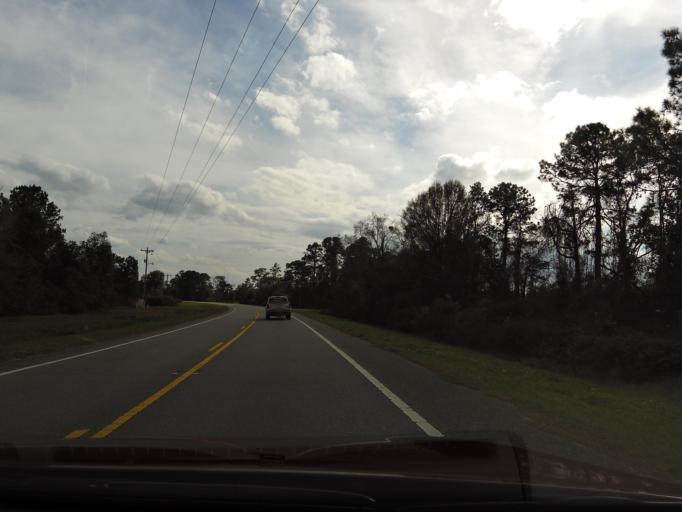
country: US
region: Florida
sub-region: Volusia County
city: De Leon Springs
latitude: 29.1979
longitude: -81.3139
